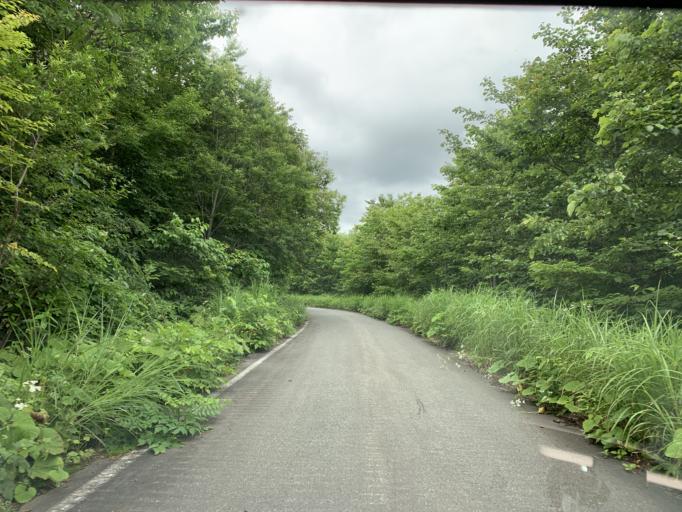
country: JP
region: Iwate
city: Ichinoseki
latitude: 38.9337
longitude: 140.8852
